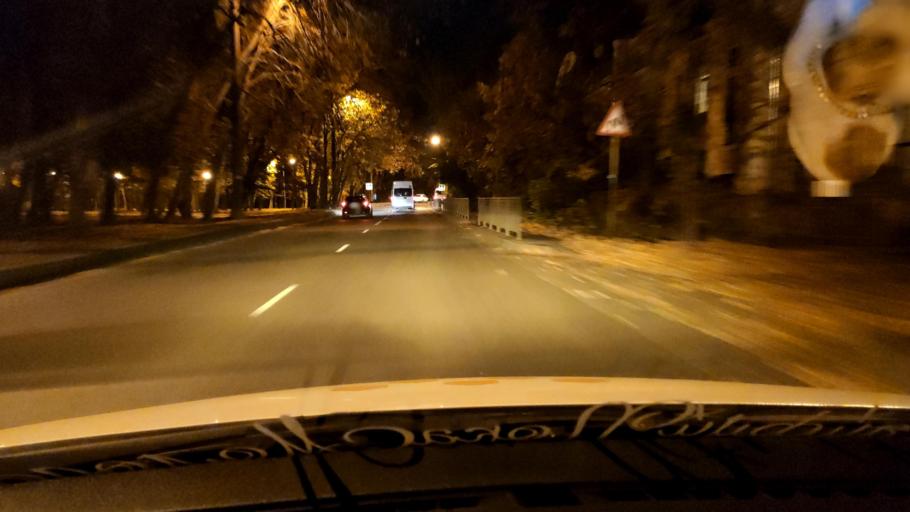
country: RU
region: Voronezj
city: Voronezh
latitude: 51.7102
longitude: 39.2262
